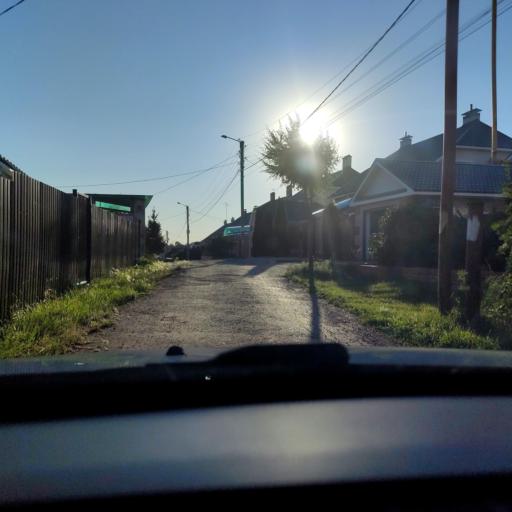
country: RU
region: Samara
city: Kinel'
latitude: 53.2760
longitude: 50.5907
